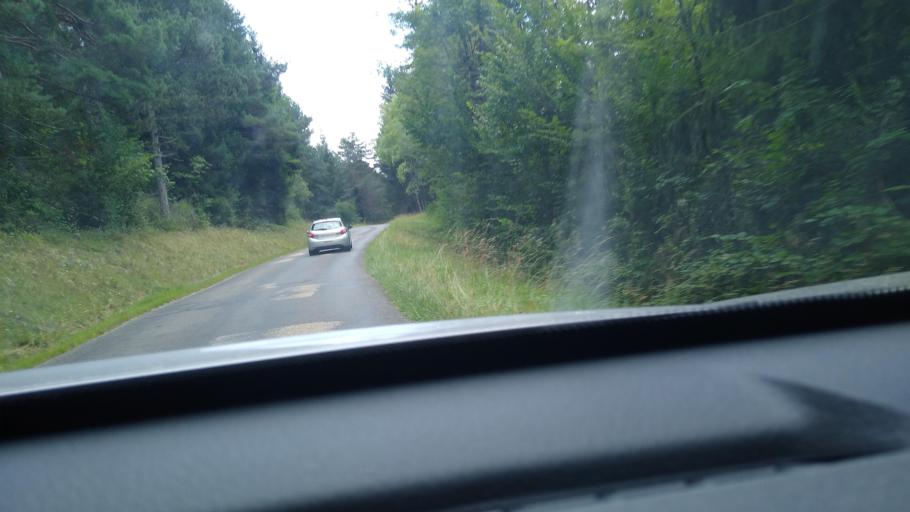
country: FR
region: Rhone-Alpes
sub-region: Departement de l'Ain
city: Saint-Martin-du-Frene
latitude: 46.1329
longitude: 5.5563
